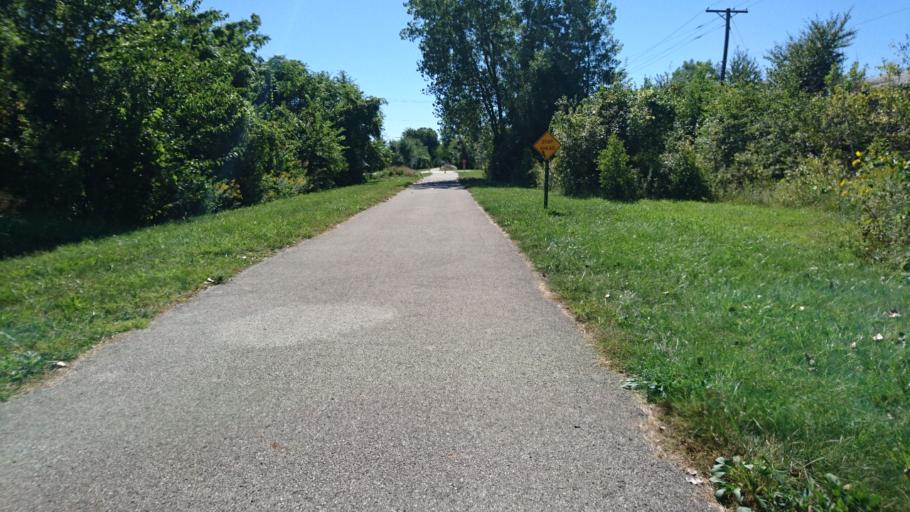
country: US
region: Illinois
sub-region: Cook County
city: Lansing
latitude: 41.5750
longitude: -87.5449
